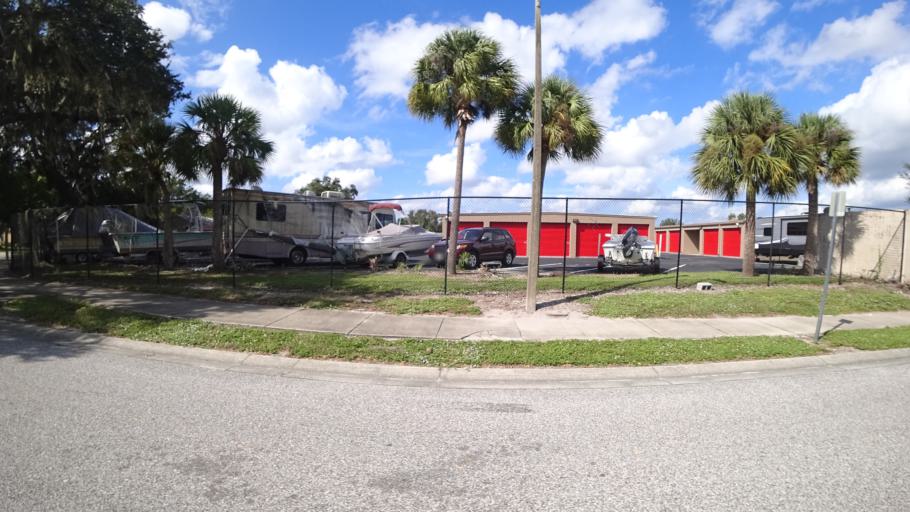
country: US
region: Florida
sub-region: Manatee County
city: Ellenton
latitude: 27.4944
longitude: -82.5276
